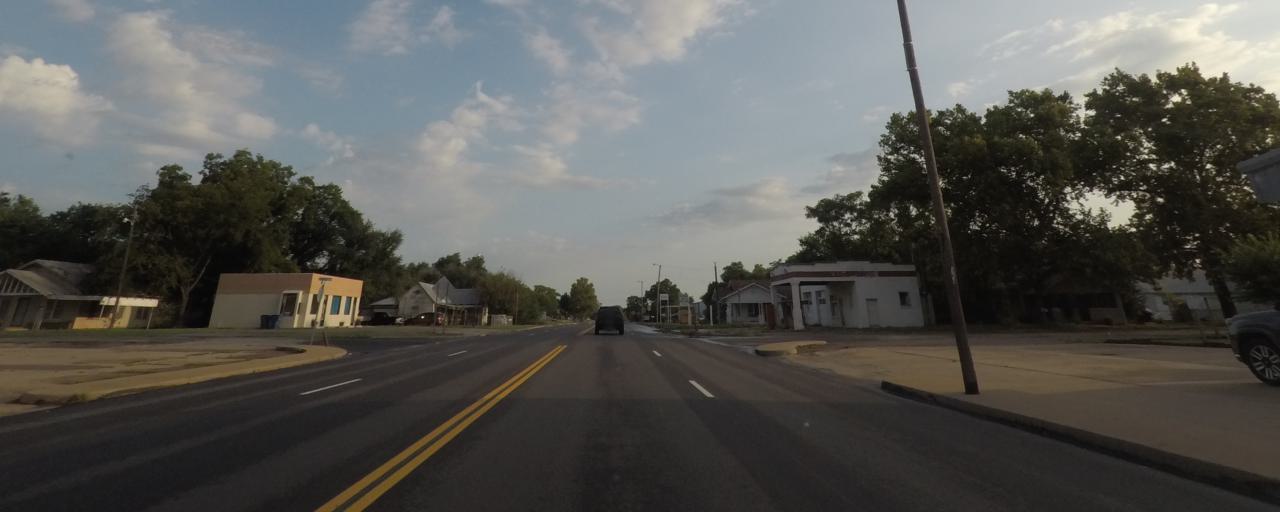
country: US
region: Oklahoma
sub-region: Stephens County
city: Comanche
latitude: 34.3697
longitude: -97.9642
